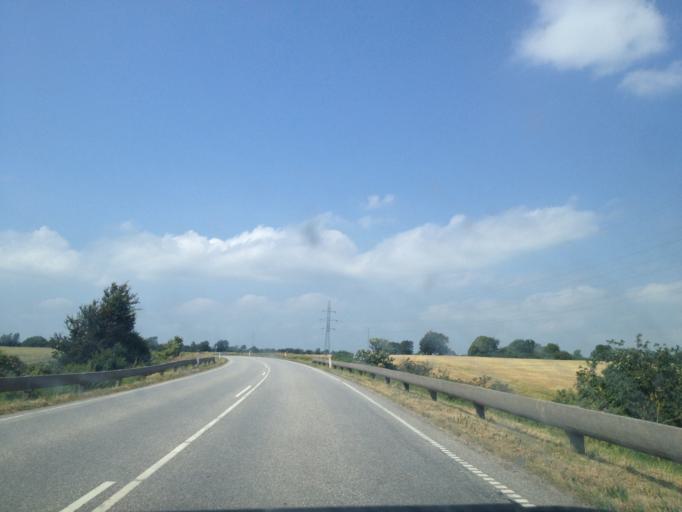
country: DK
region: South Denmark
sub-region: Haderslev Kommune
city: Vojens
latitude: 55.3336
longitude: 9.3006
